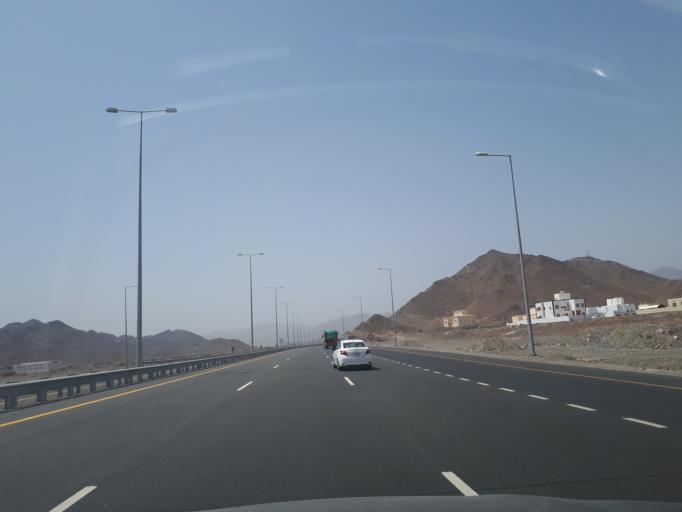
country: OM
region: Muhafazat ad Dakhiliyah
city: Bidbid
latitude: 23.3249
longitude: 58.1157
